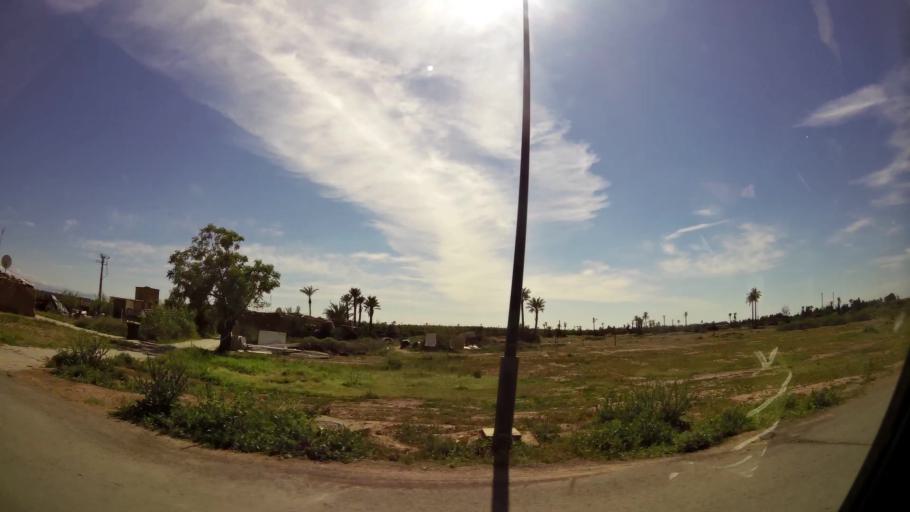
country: MA
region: Marrakech-Tensift-Al Haouz
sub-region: Marrakech
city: Marrakesh
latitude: 31.6416
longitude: -7.9439
